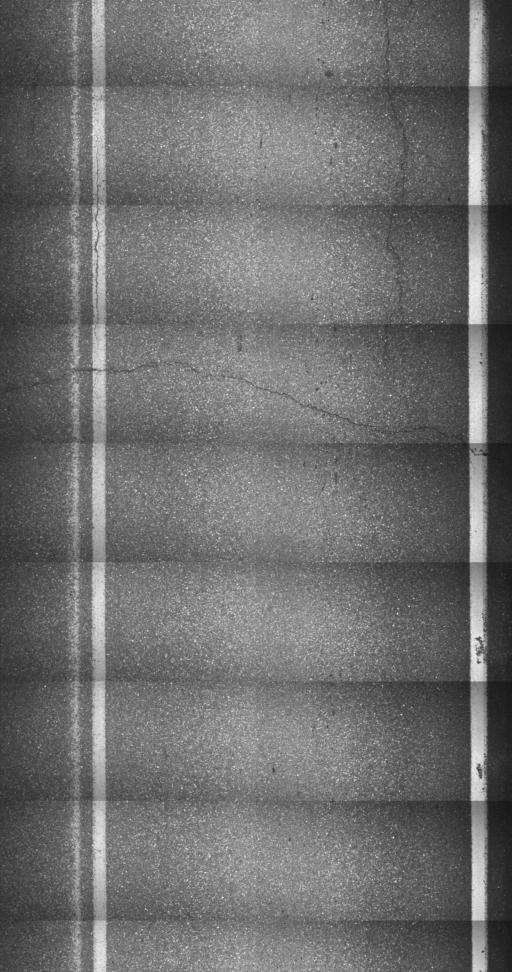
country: US
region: Vermont
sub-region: Orange County
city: Chelsea
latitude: 43.9325
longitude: -72.4662
